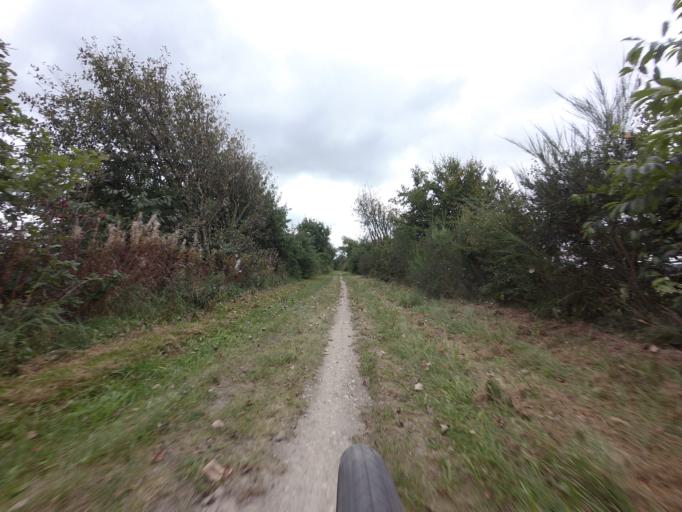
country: DK
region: Central Jutland
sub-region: Ikast-Brande Kommune
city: Brande
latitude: 55.8650
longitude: 9.0234
